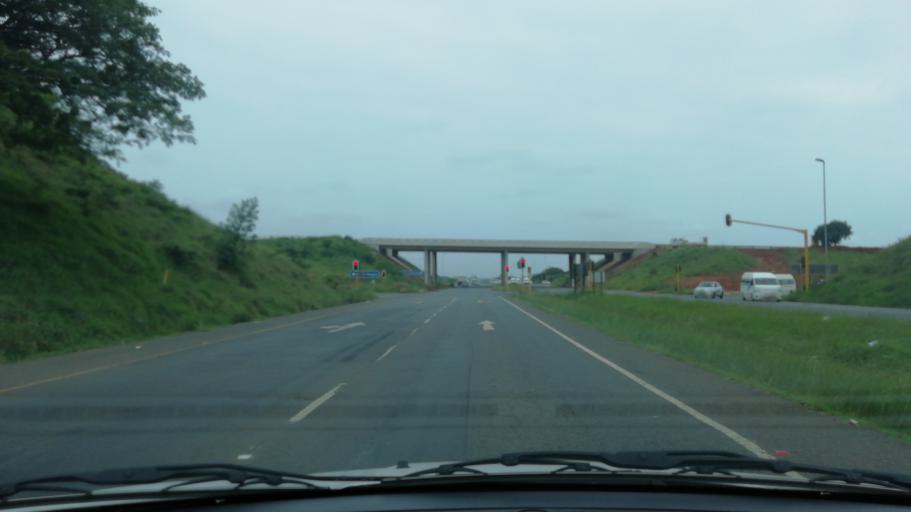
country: ZA
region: KwaZulu-Natal
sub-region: uThungulu District Municipality
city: Empangeni
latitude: -28.7684
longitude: 31.9290
